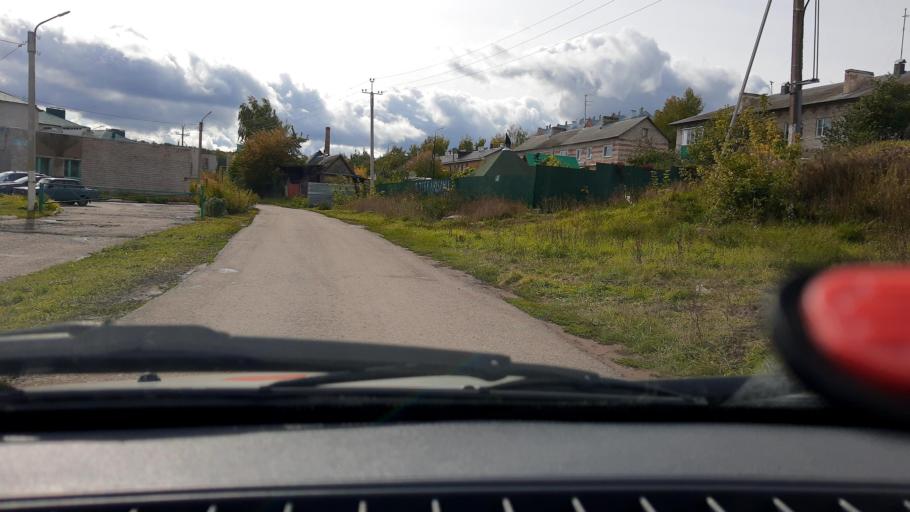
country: RU
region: Bashkortostan
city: Belebey
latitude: 54.1020
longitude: 54.1135
